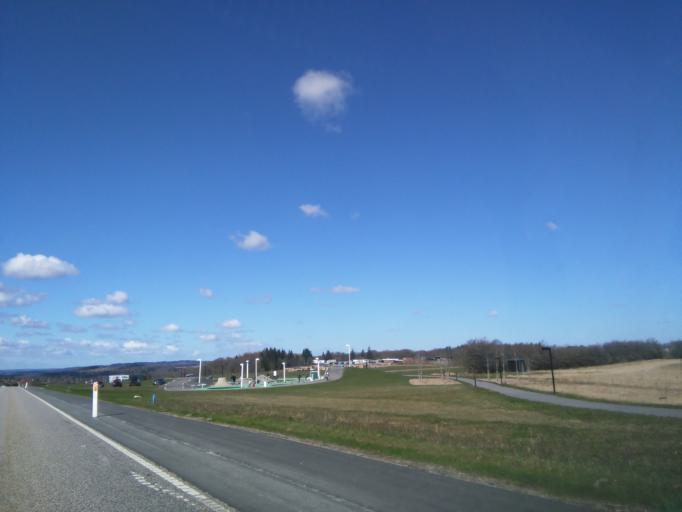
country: DK
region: Central Jutland
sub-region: Skanderborg Kommune
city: Ry
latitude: 56.0873
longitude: 9.7940
